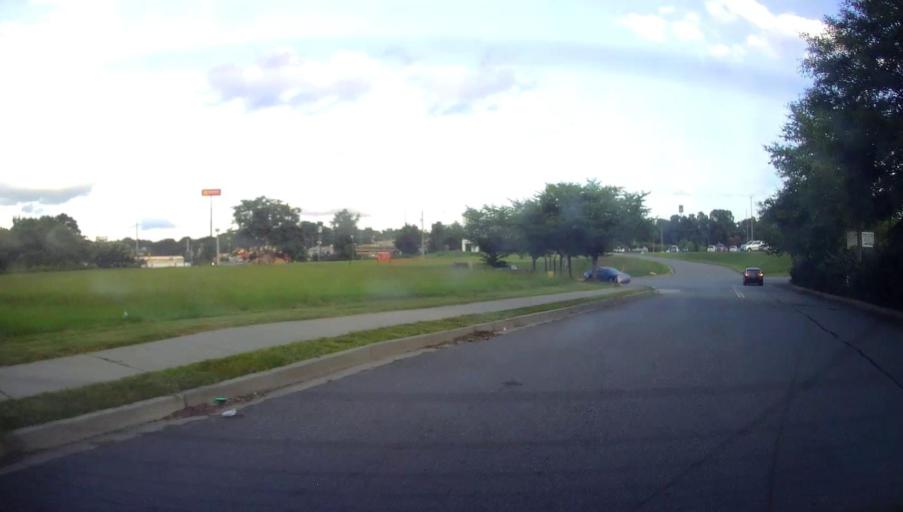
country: US
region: Georgia
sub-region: Monroe County
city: Forsyth
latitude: 33.0413
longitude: -83.9415
